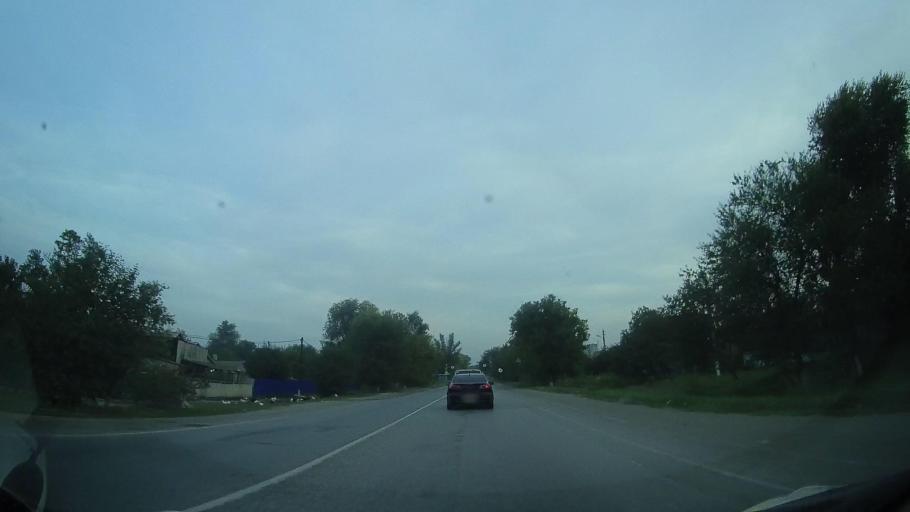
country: RU
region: Rostov
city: Kirovskaya
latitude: 46.9854
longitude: 40.0299
